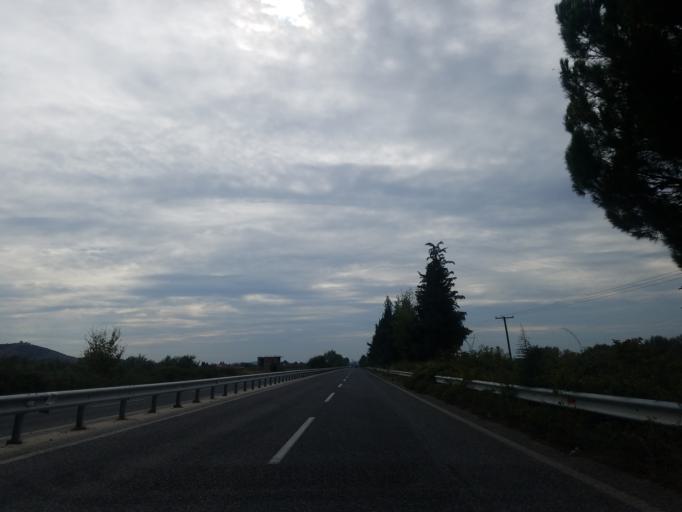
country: GR
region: Thessaly
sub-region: Trikala
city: Vasiliki
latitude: 39.6426
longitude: 21.6920
